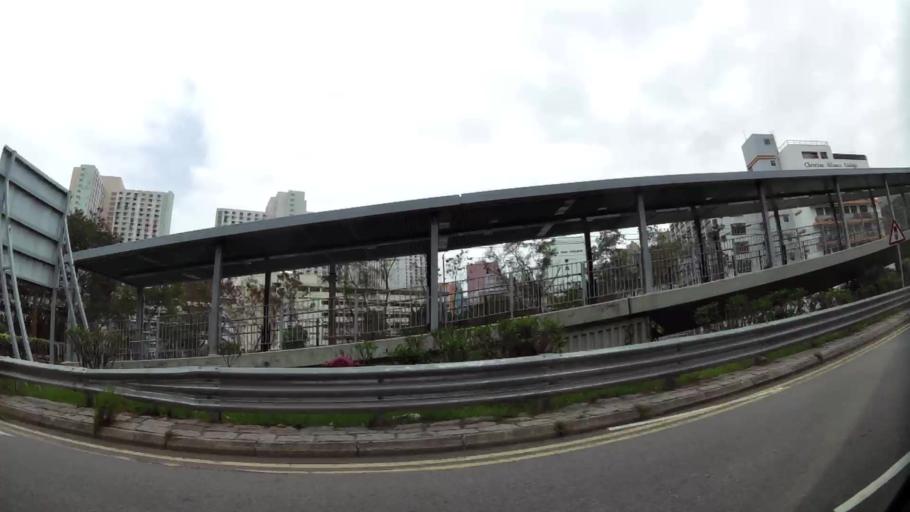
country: HK
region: Tuen Mun
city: Tuen Mun
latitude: 22.4047
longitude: 113.9681
